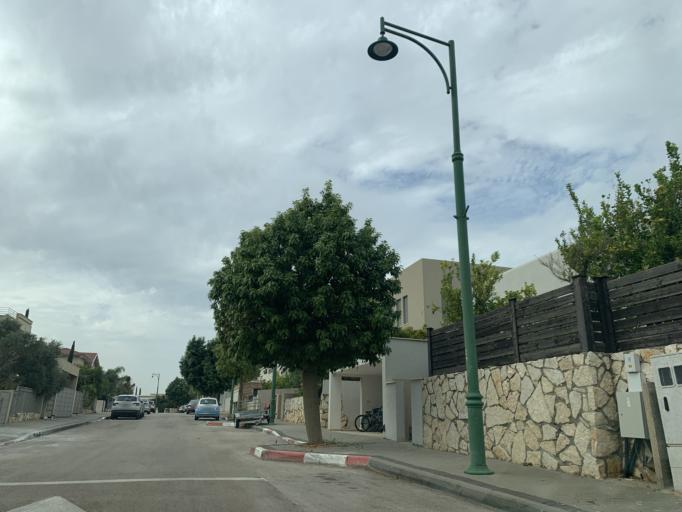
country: IL
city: Nirit
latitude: 32.1496
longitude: 34.9870
